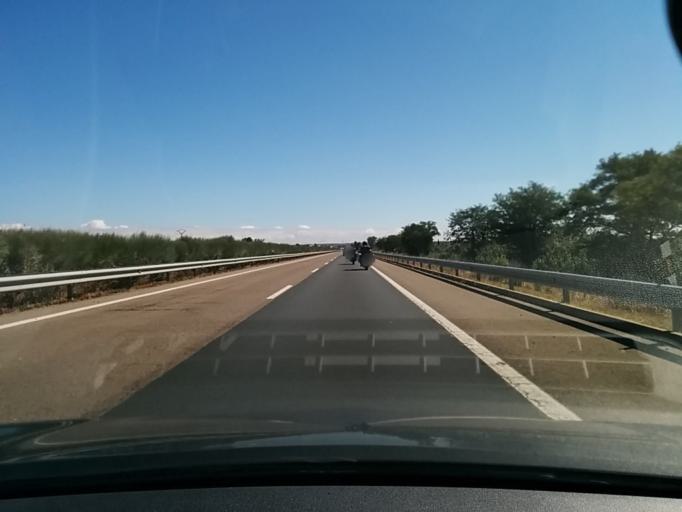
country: ES
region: Aragon
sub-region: Provincia de Huesca
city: Almudebar
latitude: 42.0266
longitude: -0.5980
